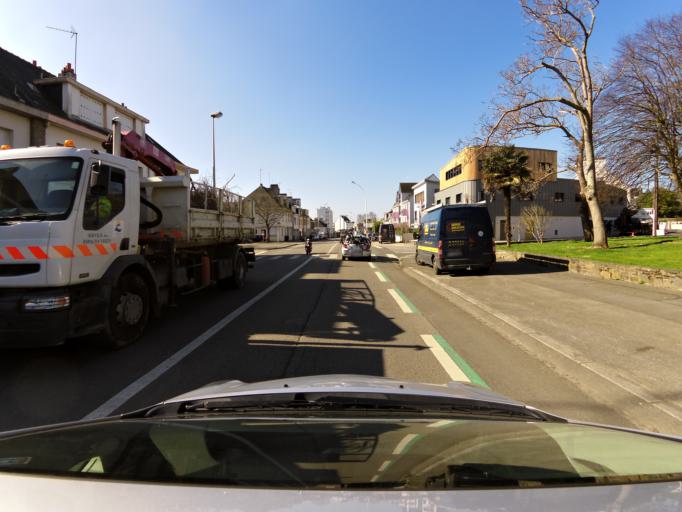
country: FR
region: Brittany
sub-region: Departement du Morbihan
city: Lorient
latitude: 47.7506
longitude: -3.3725
